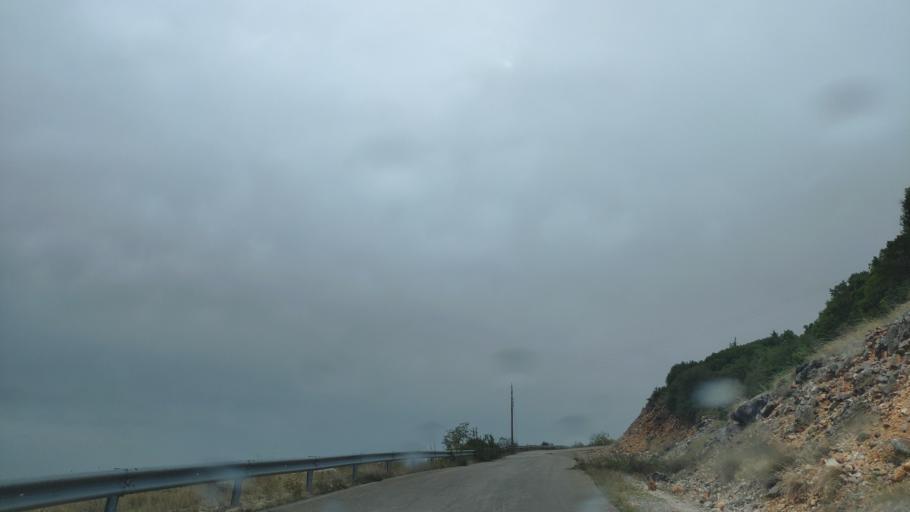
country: GR
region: Epirus
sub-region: Nomos Thesprotias
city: Paramythia
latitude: 39.4555
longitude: 20.6689
